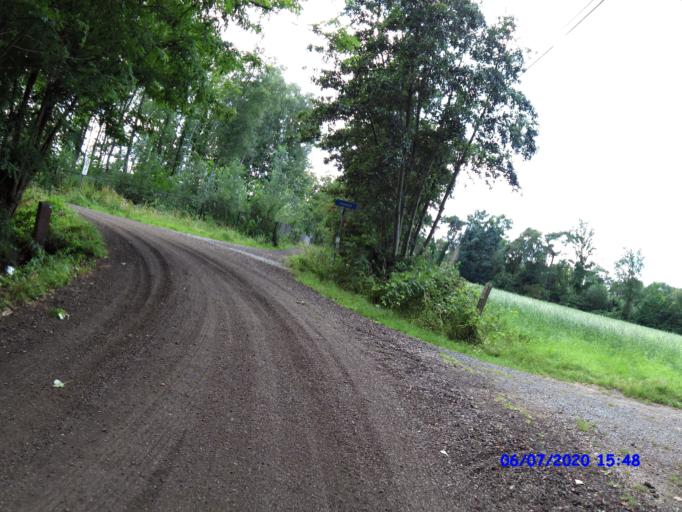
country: BE
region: Flanders
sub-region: Provincie Antwerpen
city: Balen
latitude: 51.1649
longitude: 5.1518
